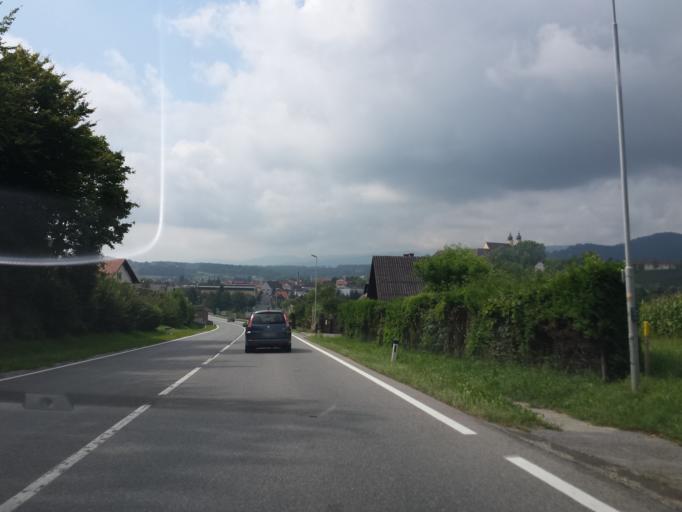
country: AT
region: Styria
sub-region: Politischer Bezirk Deutschlandsberg
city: Stainz
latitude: 46.9007
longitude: 15.2716
